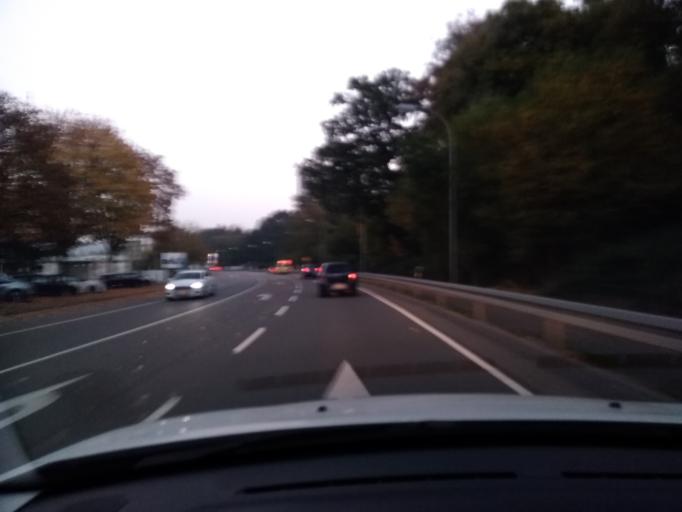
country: FR
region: Lorraine
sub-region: Departement de la Moselle
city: Alsting
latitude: 49.1997
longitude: 7.0168
